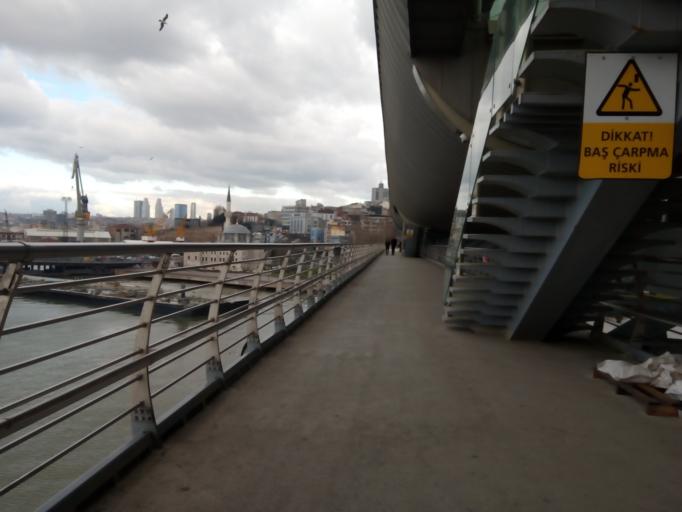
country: TR
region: Istanbul
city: Eminoenue
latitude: 41.0232
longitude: 28.9666
